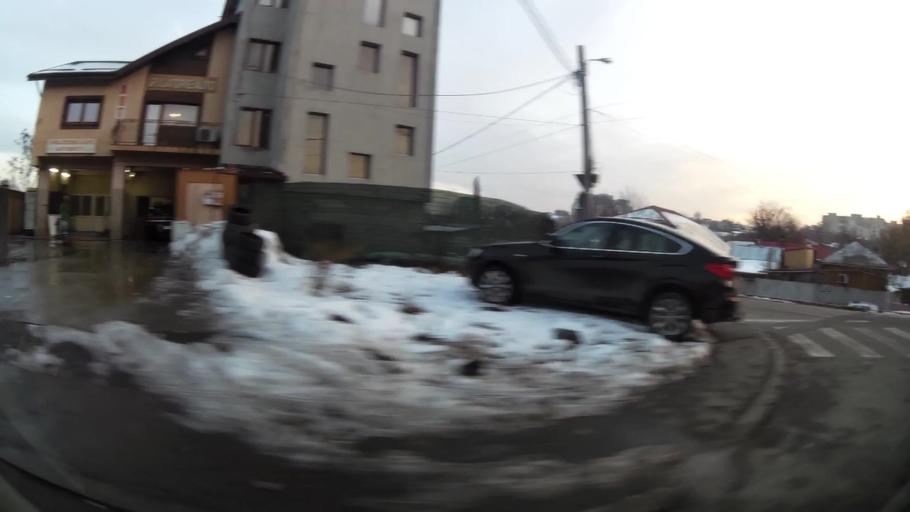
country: RO
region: Ilfov
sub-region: Comuna Fundeni-Dobroesti
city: Fundeni
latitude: 44.4616
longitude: 26.1432
